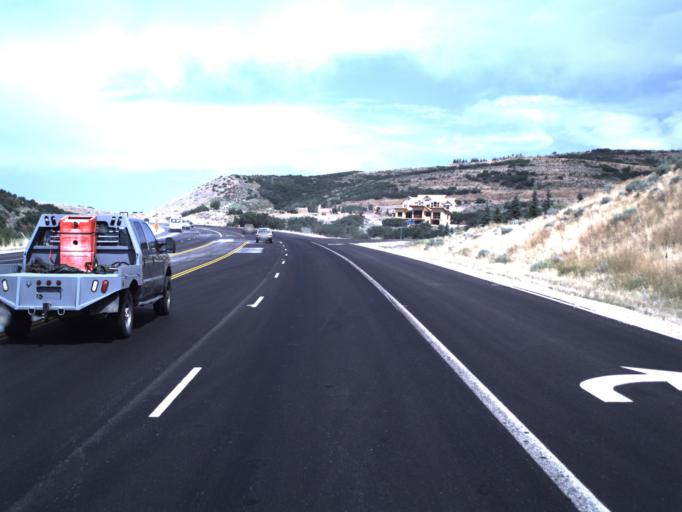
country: US
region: Utah
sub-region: Summit County
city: Park City
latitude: 40.6665
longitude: -111.4193
